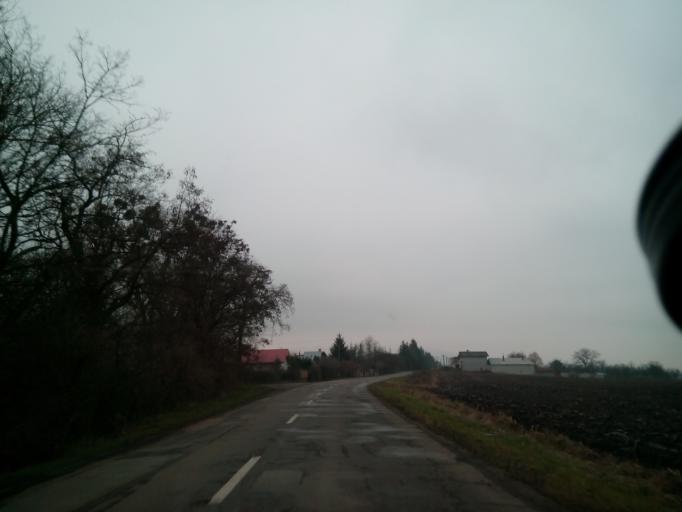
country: SK
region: Kosicky
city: Kosice
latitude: 48.7173
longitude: 21.4390
